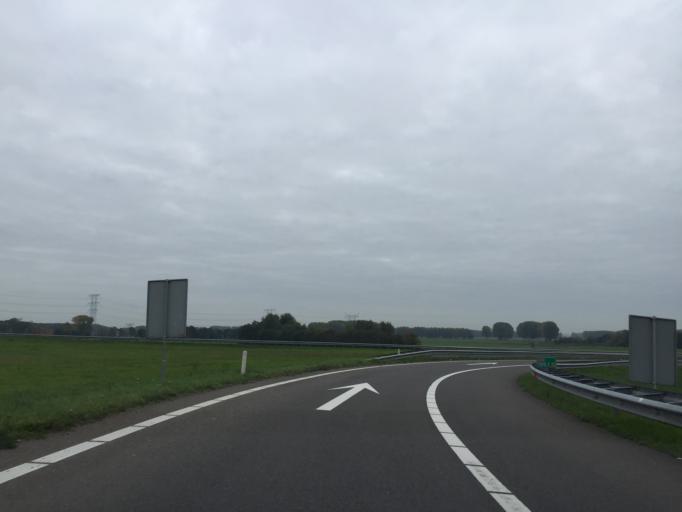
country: NL
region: North Brabant
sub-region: Gemeente Geertruidenberg
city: Geertruidenberg
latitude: 51.6798
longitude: 4.8463
